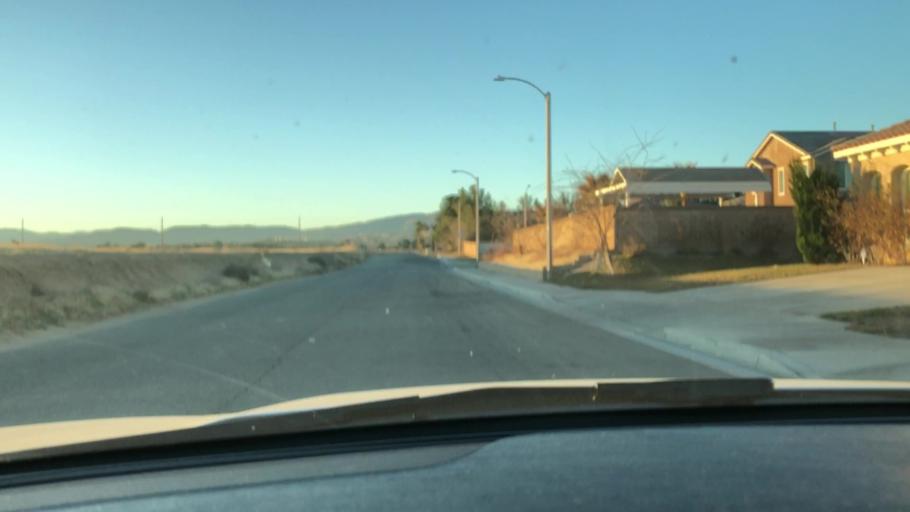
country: US
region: California
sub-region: Los Angeles County
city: Quartz Hill
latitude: 34.6788
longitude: -118.2059
